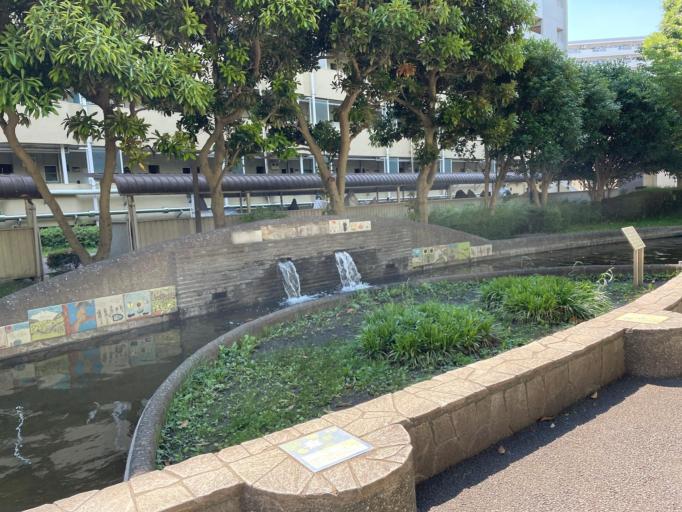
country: JP
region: Tokyo
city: Mitaka-shi
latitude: 35.6574
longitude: 139.6214
